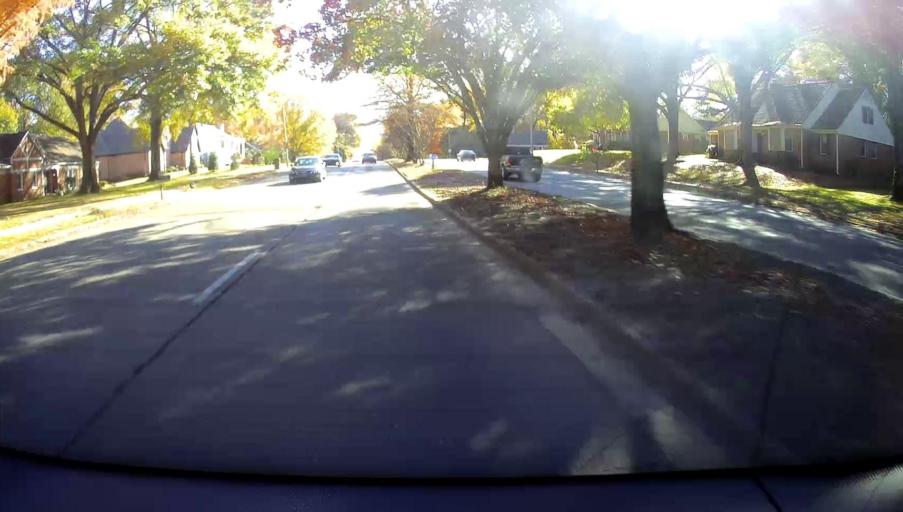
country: US
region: Tennessee
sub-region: Shelby County
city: Germantown
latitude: 35.0921
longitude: -89.8402
